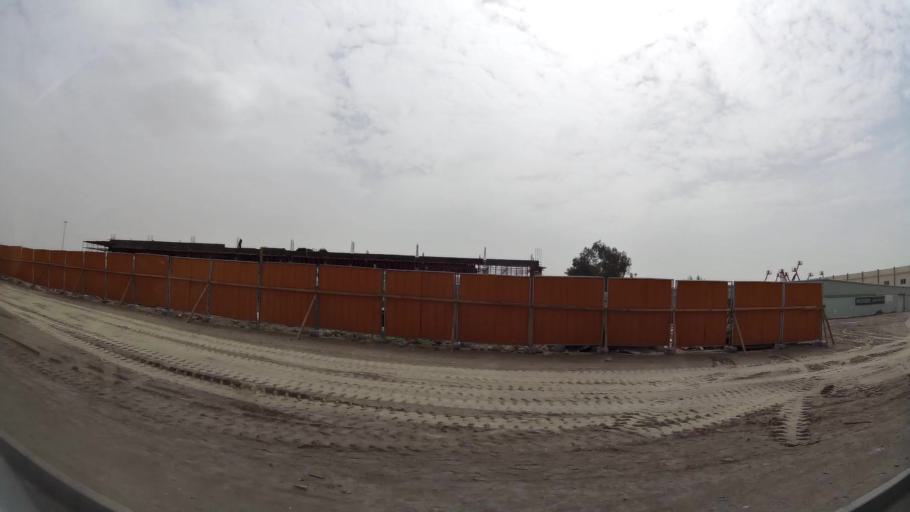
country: AE
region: Abu Dhabi
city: Abu Dhabi
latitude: 24.3533
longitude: 54.4713
